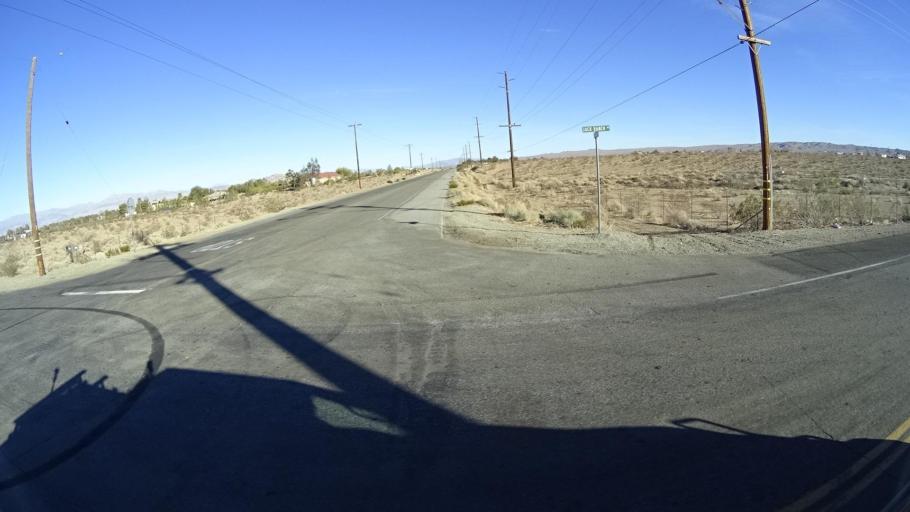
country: US
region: California
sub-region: Kern County
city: China Lake Acres
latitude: 35.6225
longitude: -117.7230
